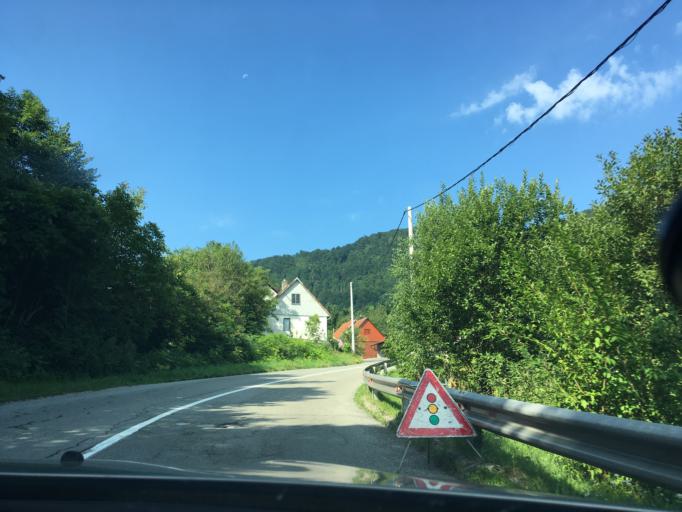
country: HR
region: Primorsko-Goranska
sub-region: Grad Delnice
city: Delnice
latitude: 45.4178
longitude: 14.8225
